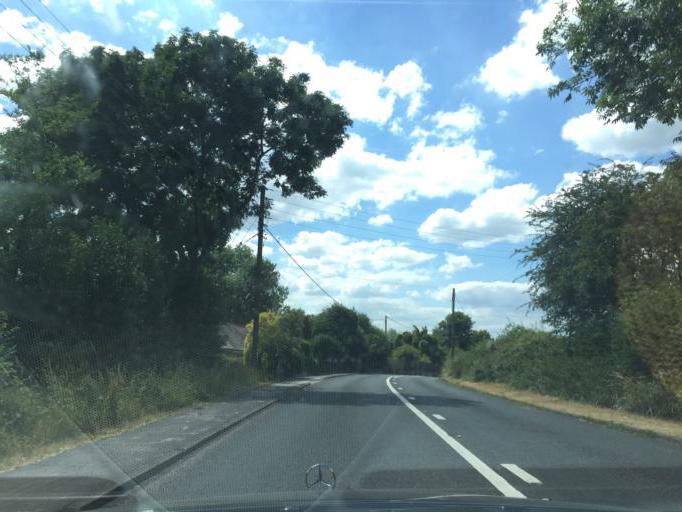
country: GB
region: England
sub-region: Leicestershire
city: Hinckley
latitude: 52.4909
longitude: -1.3628
